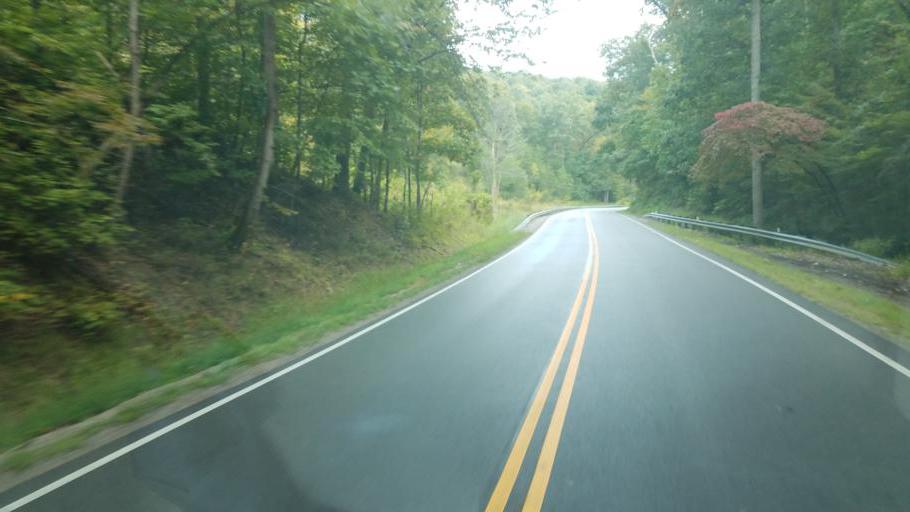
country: US
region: Ohio
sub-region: Scioto County
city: Sciotodale
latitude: 38.8742
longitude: -82.8253
